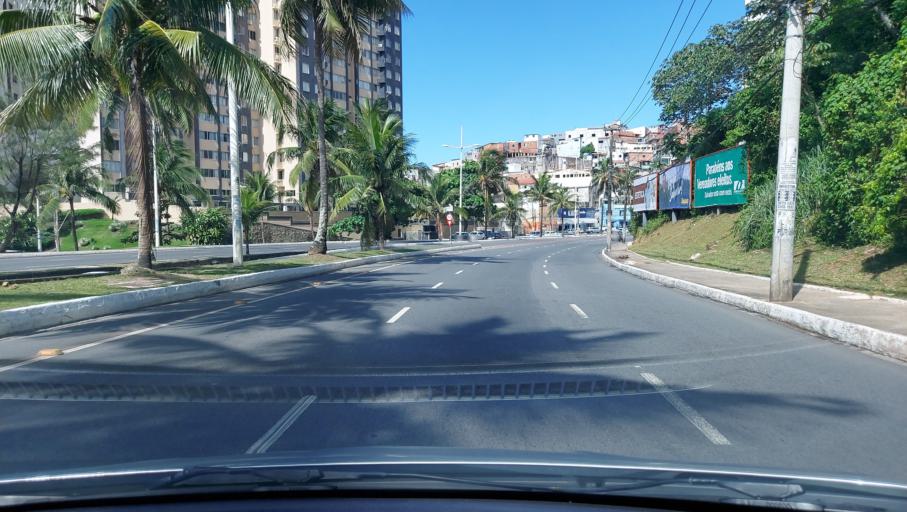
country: BR
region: Bahia
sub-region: Salvador
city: Salvador
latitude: -13.0086
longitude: -38.4966
